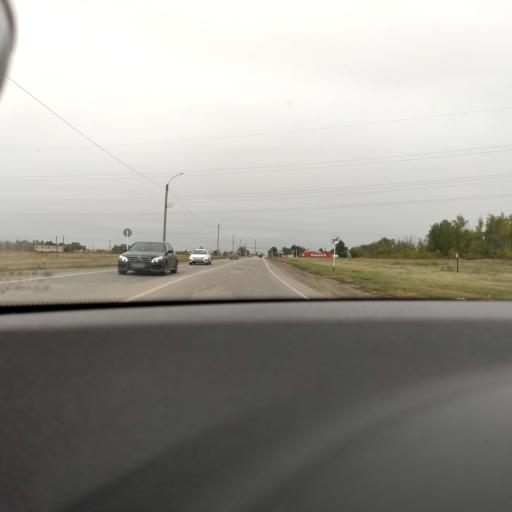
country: RU
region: Samara
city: Krasnyy Yar
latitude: 53.4748
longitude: 50.3912
